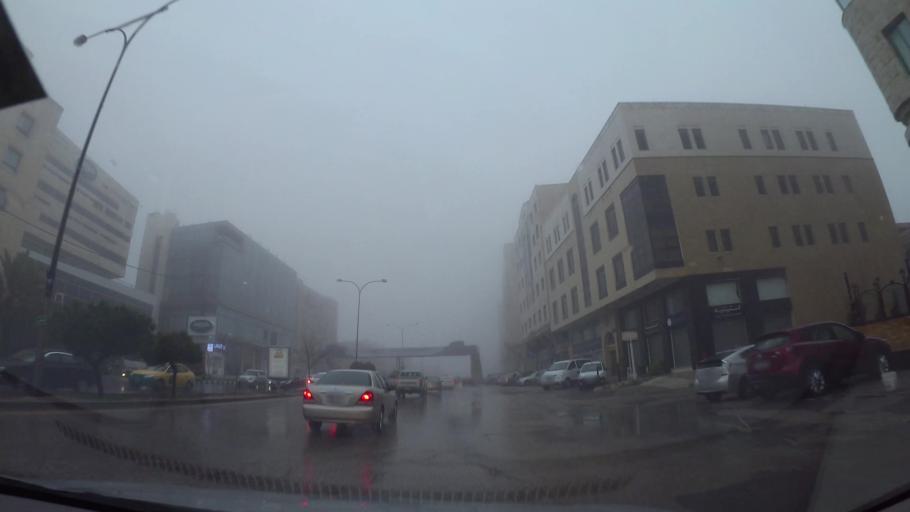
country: JO
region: Amman
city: Al Jubayhah
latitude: 31.9878
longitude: 35.8668
